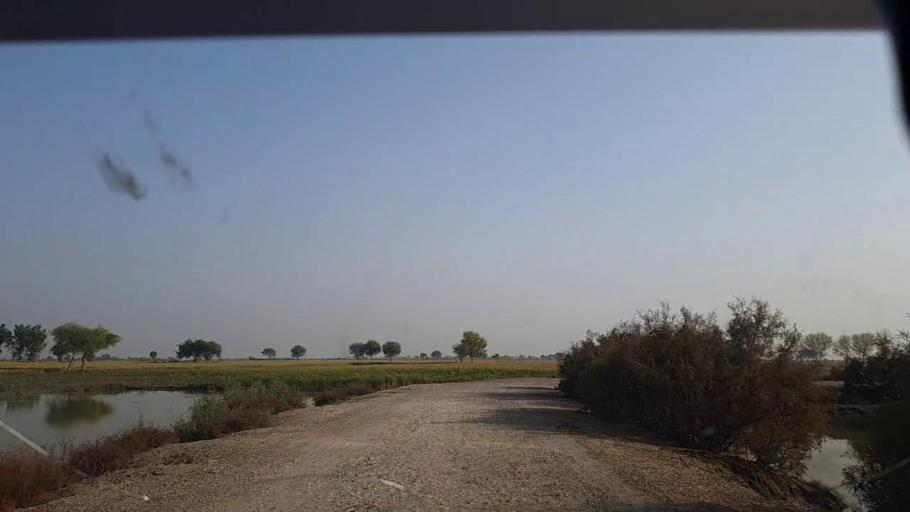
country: PK
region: Sindh
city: Shikarpur
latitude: 28.0628
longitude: 68.5485
